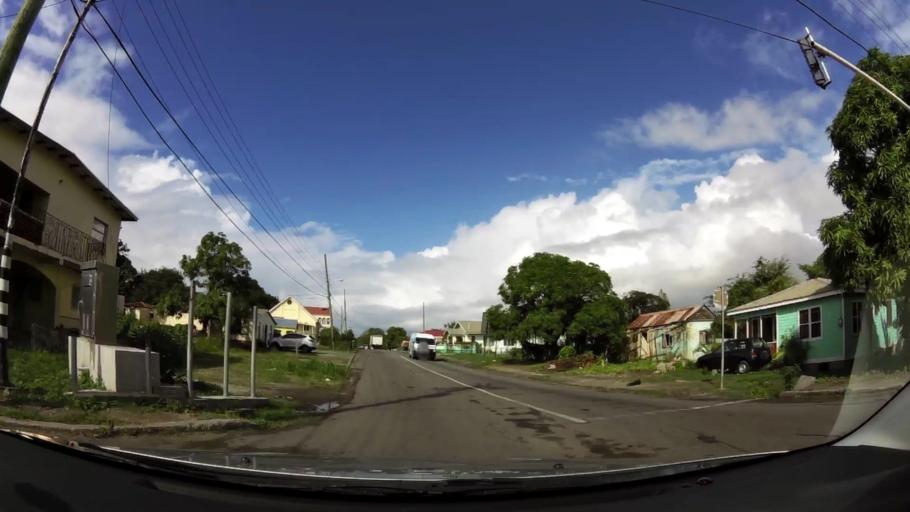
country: AG
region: Saint John
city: Saint John's
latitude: 17.1178
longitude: -61.8283
